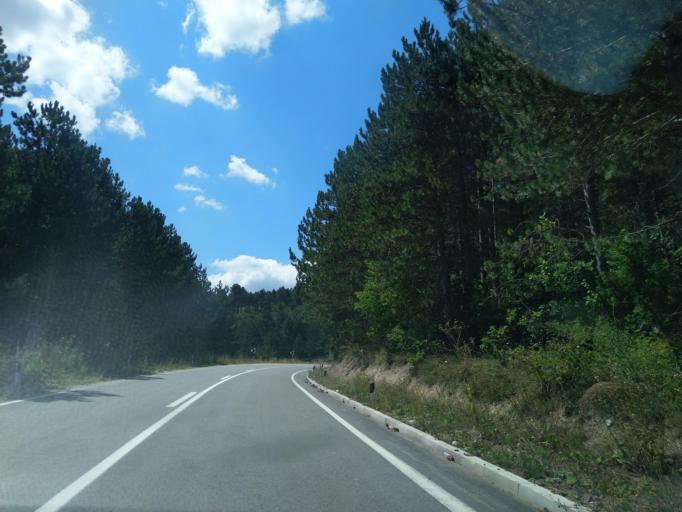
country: RS
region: Central Serbia
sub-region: Zlatiborski Okrug
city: Sjenica
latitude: 43.3061
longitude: 19.9029
